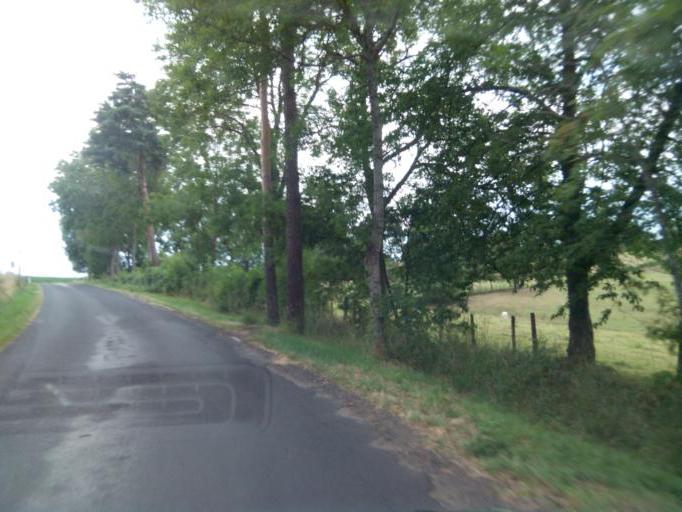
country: FR
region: Rhone-Alpes
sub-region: Departement de la Loire
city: Usson-en-Forez
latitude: 45.3714
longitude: 3.9566
